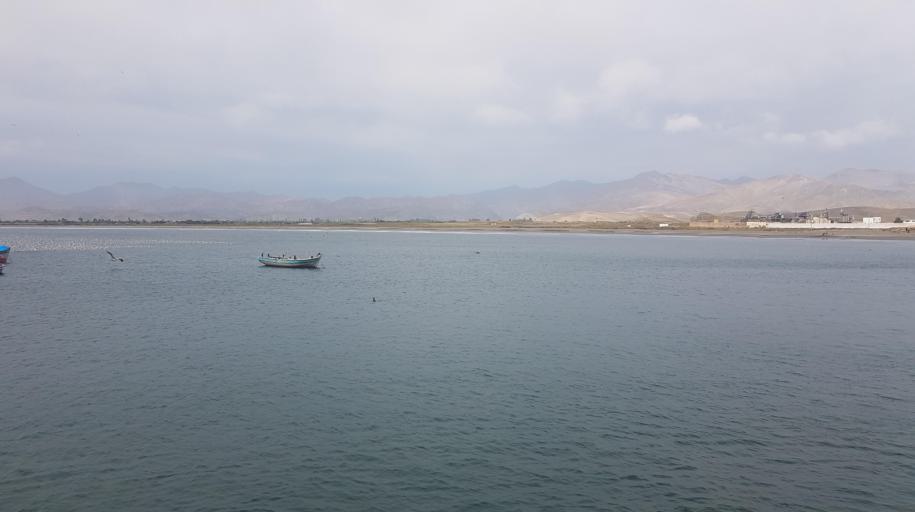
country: PE
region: Ancash
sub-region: Provincia de Huarmey
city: Huarmey
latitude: -10.0971
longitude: -78.1711
